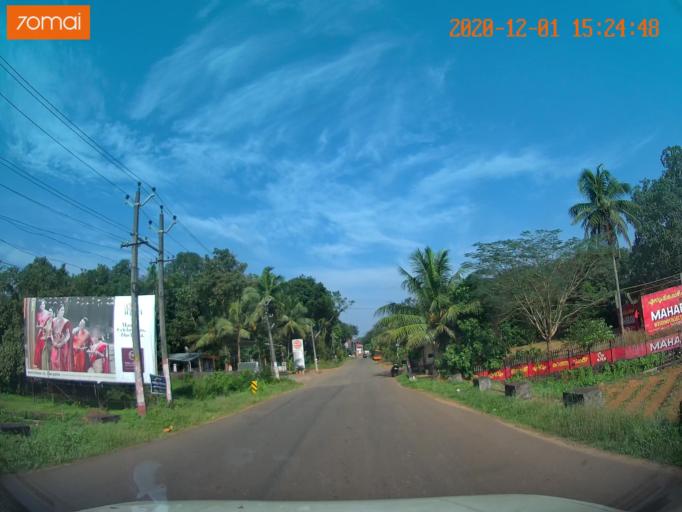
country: IN
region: Kerala
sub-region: Ernakulam
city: Muvattupuzha
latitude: 9.9549
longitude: 76.5582
